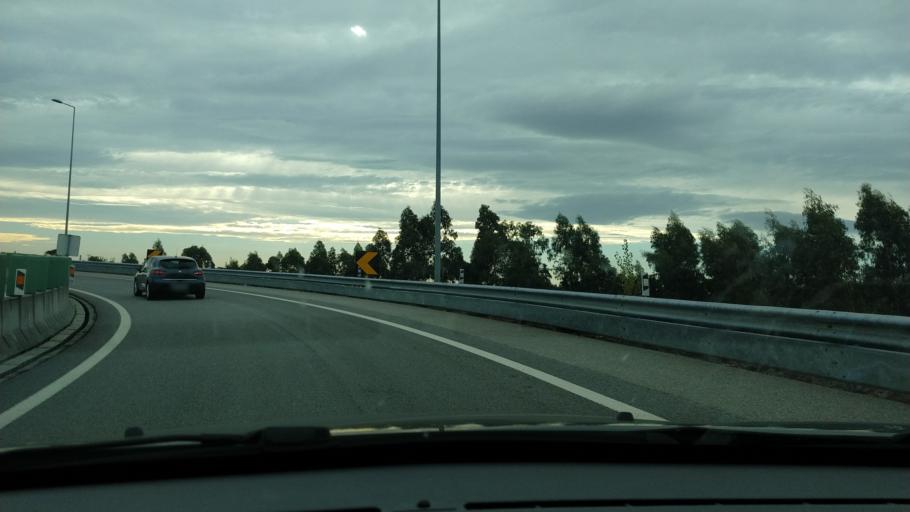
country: PT
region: Coimbra
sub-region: Figueira da Foz
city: Alhadas
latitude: 40.1522
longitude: -8.7836
